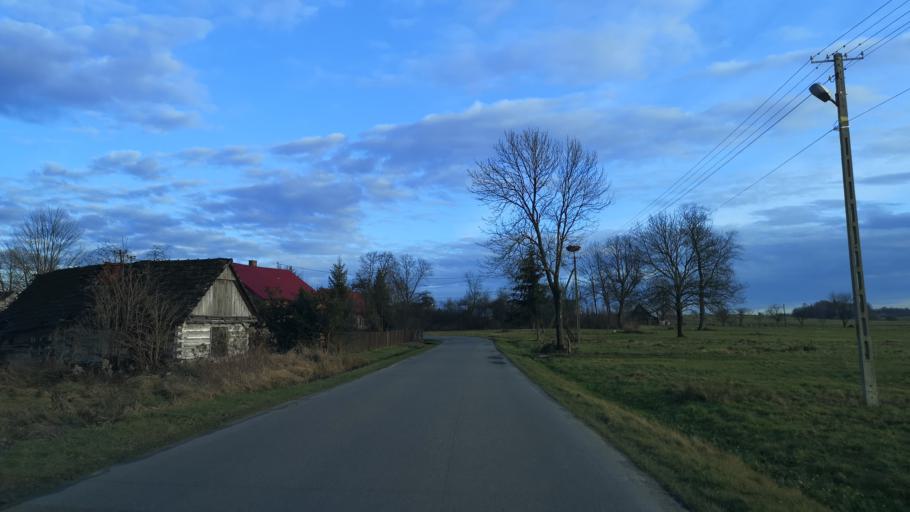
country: PL
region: Subcarpathian Voivodeship
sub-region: Powiat przeworski
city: Sieniawa
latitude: 50.2540
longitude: 22.6115
